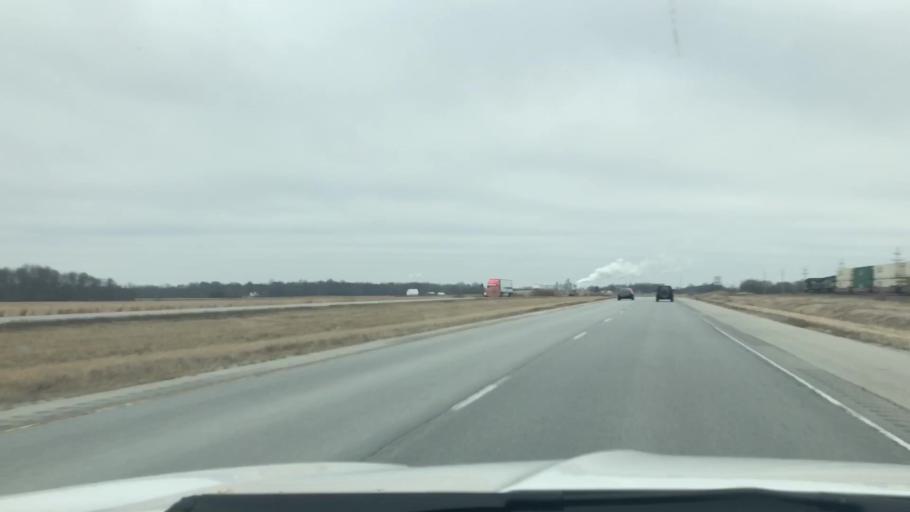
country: US
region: Indiana
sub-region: Cass County
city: Georgetown
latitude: 40.6963
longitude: -86.4706
